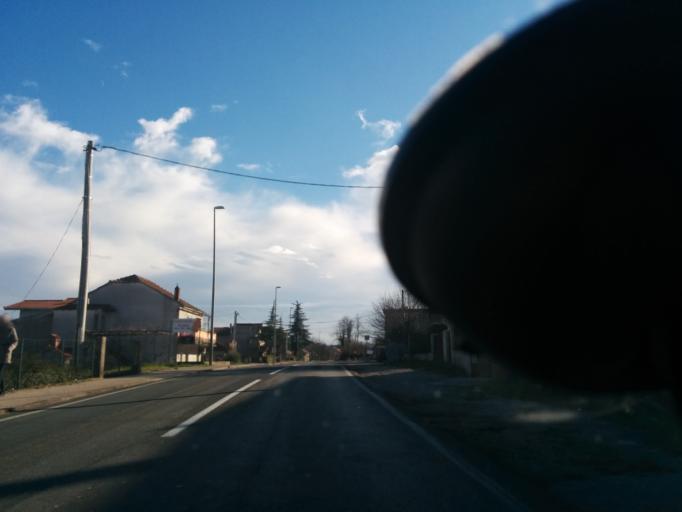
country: HR
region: Splitsko-Dalmatinska
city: Brnaze
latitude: 43.6894
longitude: 16.6473
